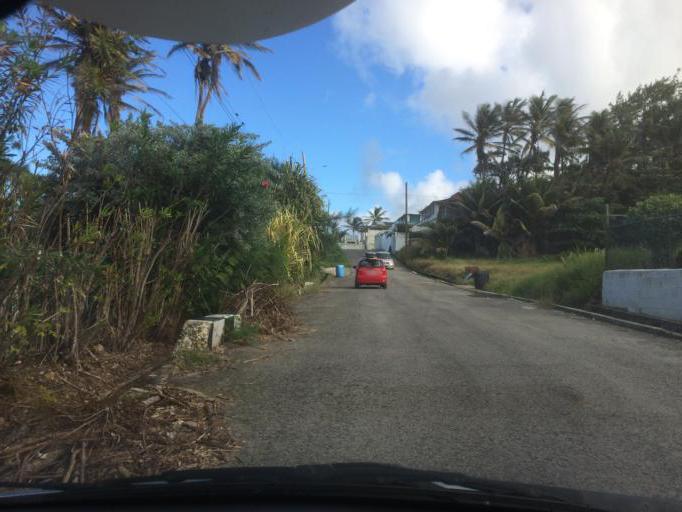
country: BB
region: Saint Joseph
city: Bathsheba
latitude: 13.2136
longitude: -59.5229
